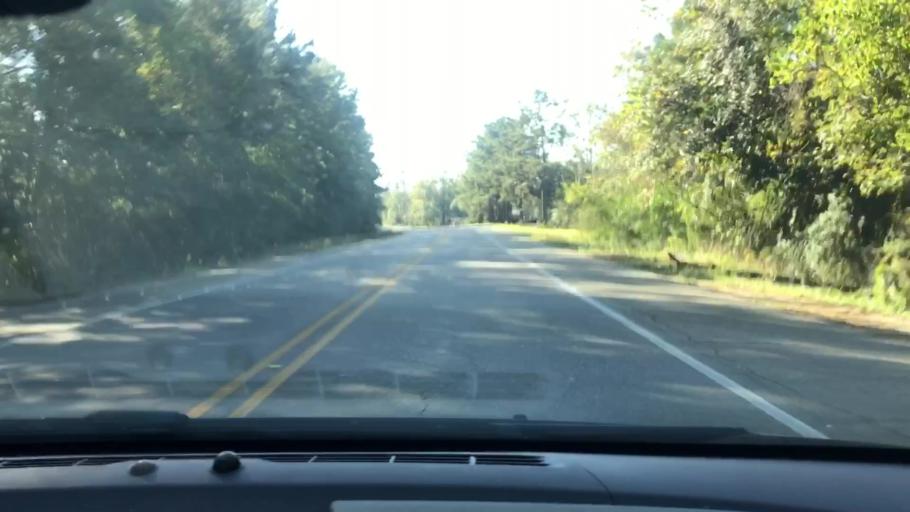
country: US
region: Louisiana
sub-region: Saint Tammany Parish
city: Pearl River
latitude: 30.4226
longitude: -89.7875
